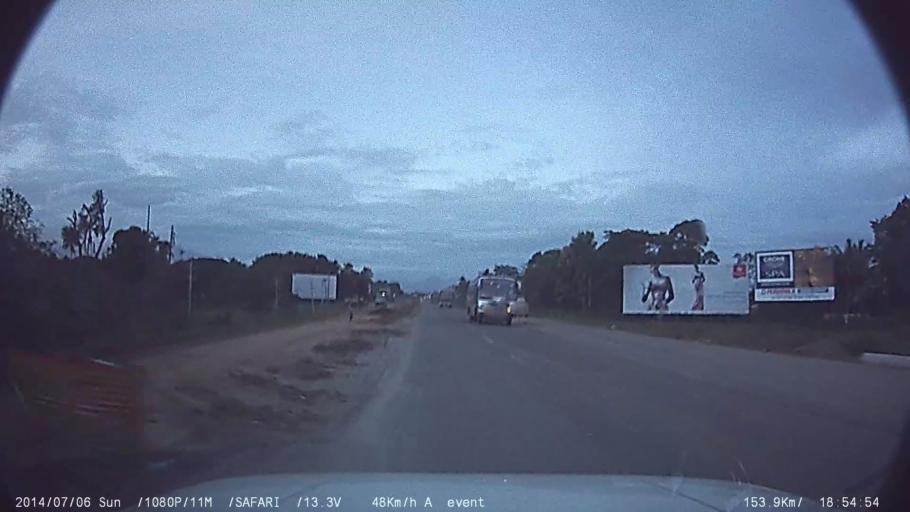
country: IN
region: Kerala
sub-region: Palakkad district
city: Palakkad
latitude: 10.7342
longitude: 76.6140
